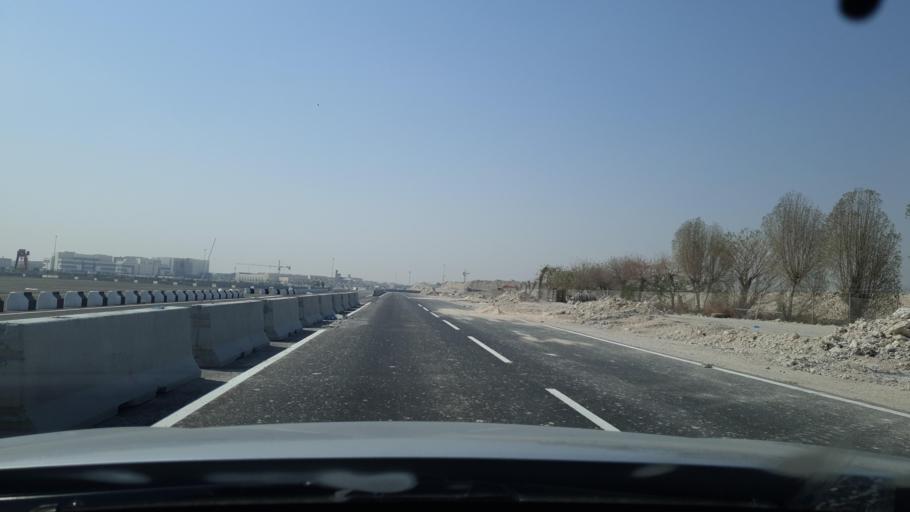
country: QA
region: Baladiyat ad Dawhah
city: Doha
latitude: 25.2253
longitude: 51.5266
